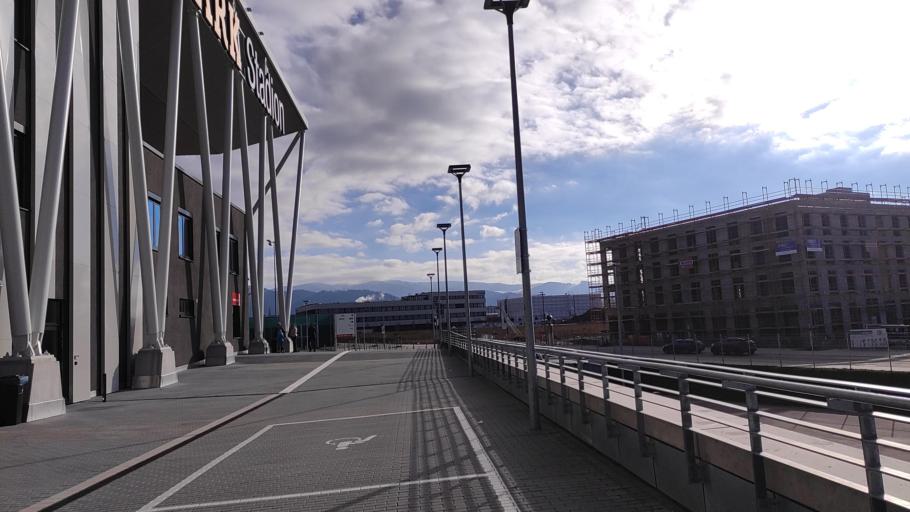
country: DE
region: Baden-Wuerttemberg
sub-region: Freiburg Region
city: Freiburg
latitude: 48.0211
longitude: 7.8288
